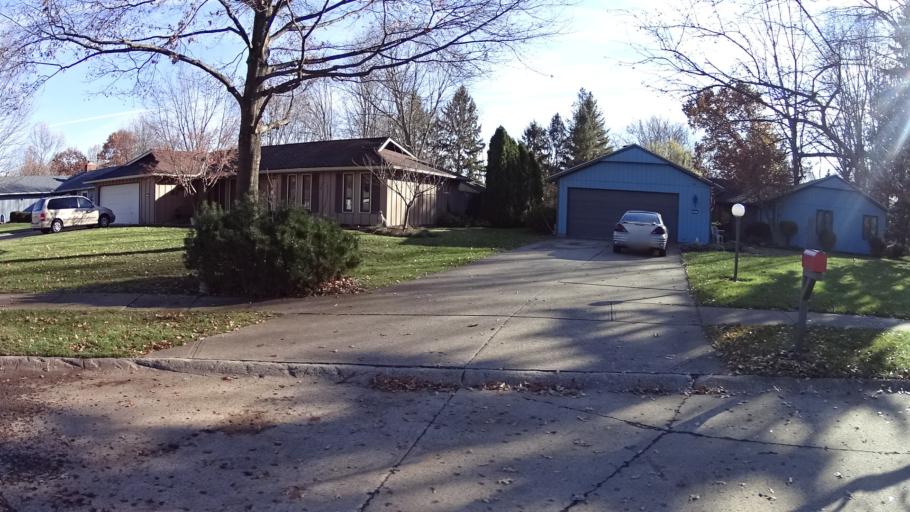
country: US
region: Ohio
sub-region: Lorain County
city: North Ridgeville
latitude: 41.4019
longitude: -81.9743
